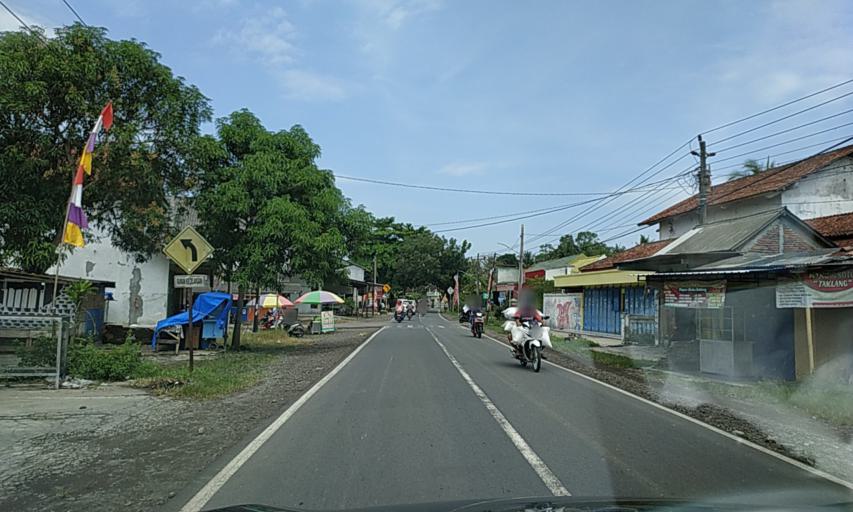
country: ID
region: Central Java
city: Sidareja
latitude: -7.4933
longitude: 108.7907
